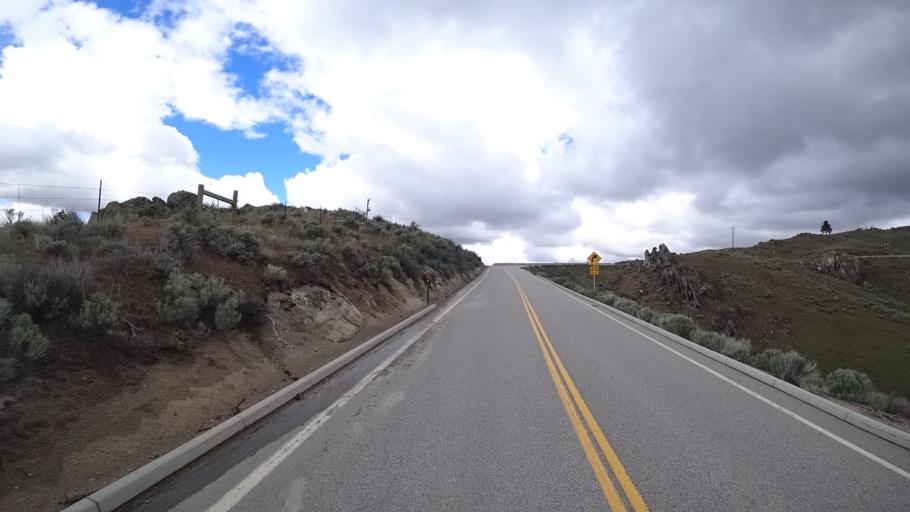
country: US
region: Idaho
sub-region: Ada County
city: Boise
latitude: 43.7128
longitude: -116.1631
